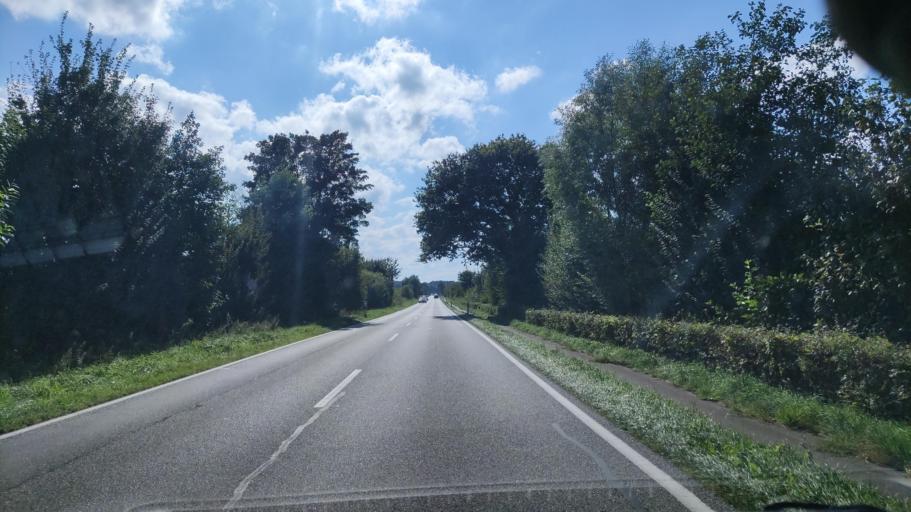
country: DE
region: Schleswig-Holstein
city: Holzbunge
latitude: 54.4045
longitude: 9.6730
